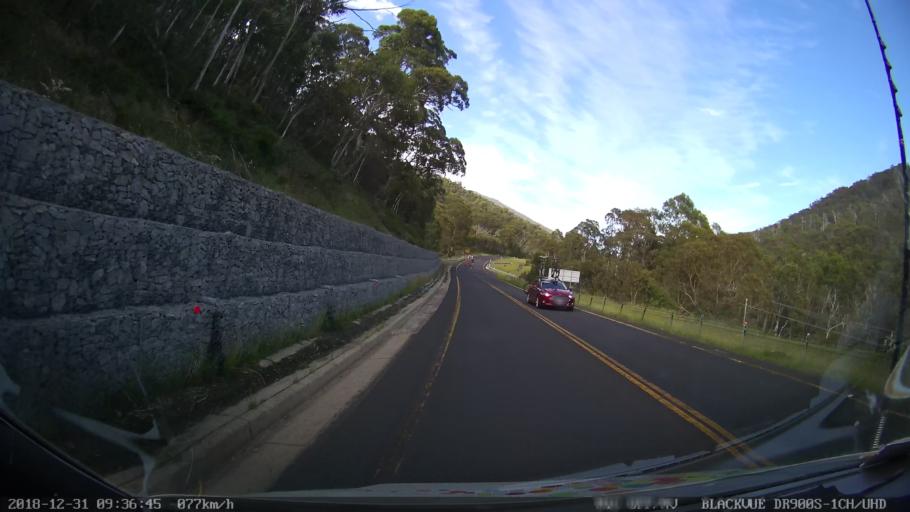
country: AU
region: New South Wales
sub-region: Snowy River
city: Jindabyne
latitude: -36.4611
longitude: 148.3833
